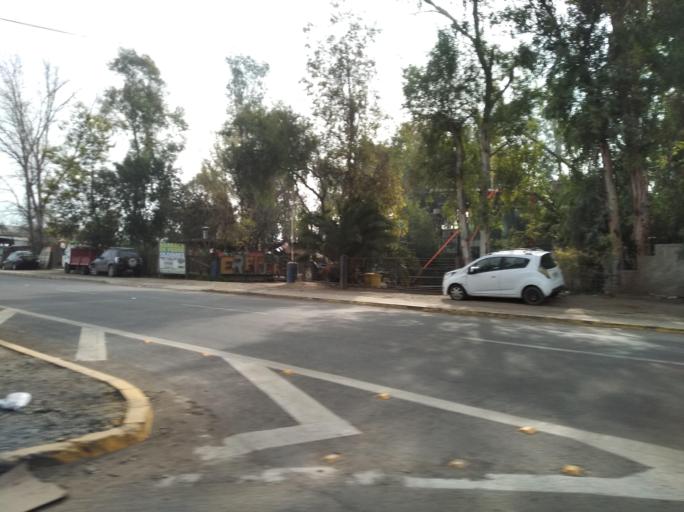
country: CL
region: Santiago Metropolitan
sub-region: Provincia de Chacabuco
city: Lampa
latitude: -33.2941
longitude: -70.8664
